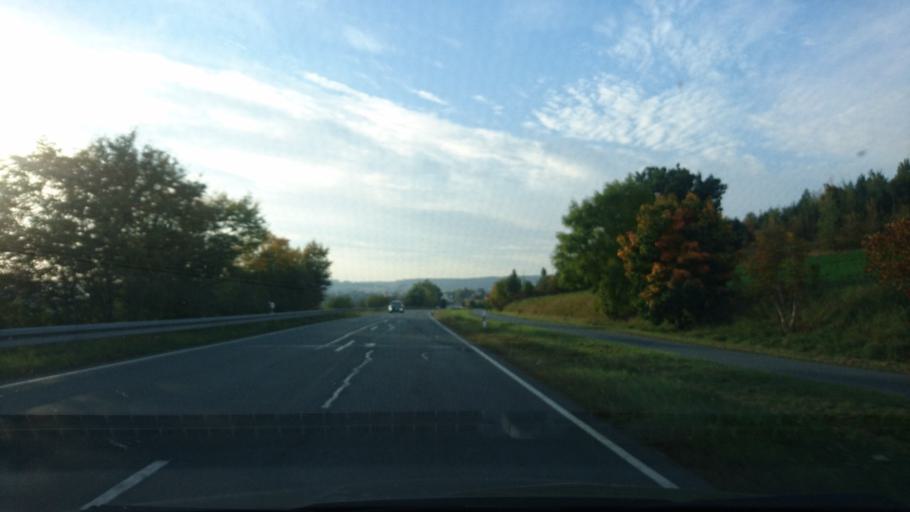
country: DE
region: Bavaria
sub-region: Upper Franconia
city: Selbitz
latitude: 50.3186
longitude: 11.7308
